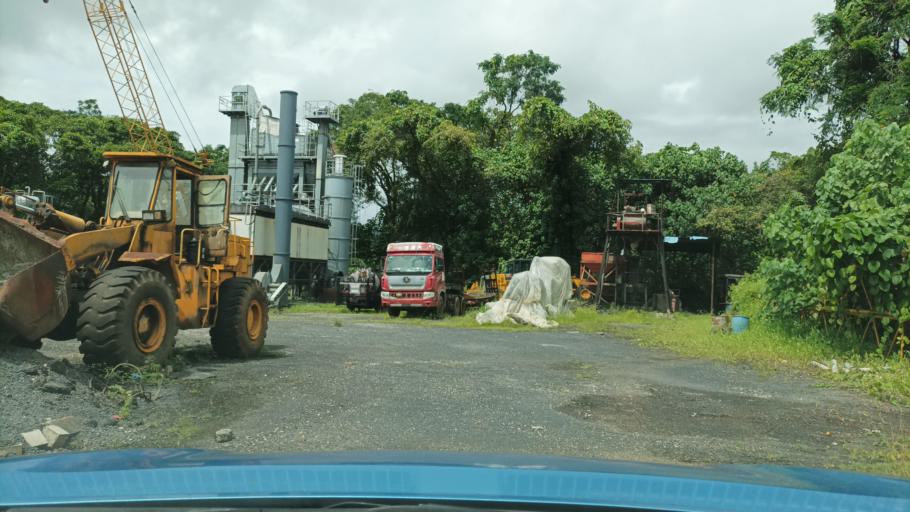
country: FM
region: Pohnpei
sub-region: Madolenihm Municipality
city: Madolenihm Municipality Government
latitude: 6.8939
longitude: 158.3148
